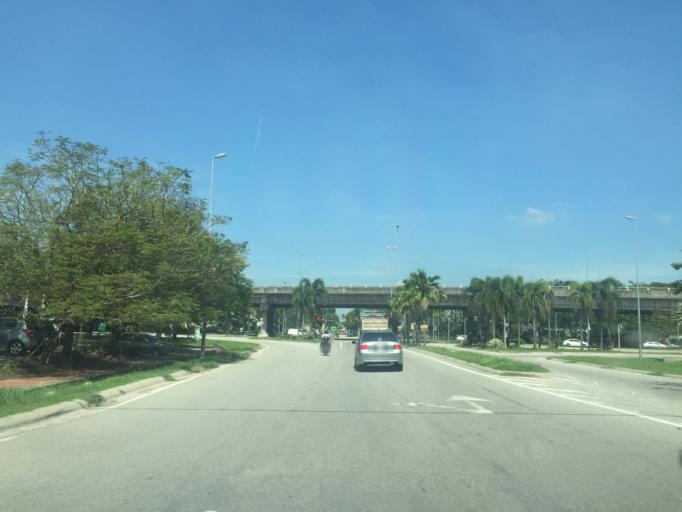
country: MY
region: Penang
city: Permatang Kuching
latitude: 5.4459
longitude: 100.3969
